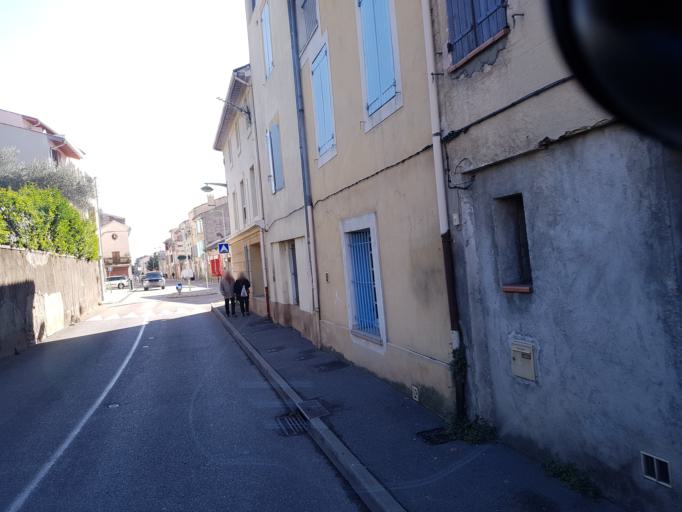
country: FR
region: Provence-Alpes-Cote d'Azur
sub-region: Departement des Alpes-de-Haute-Provence
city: Manosque
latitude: 43.8347
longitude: 5.7874
